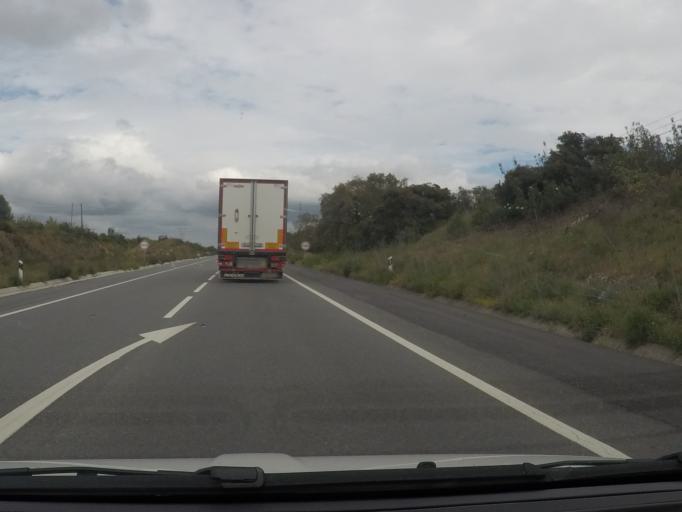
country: PT
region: Setubal
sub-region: Santiago do Cacem
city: Santiago do Cacem
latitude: 38.0709
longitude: -8.6636
